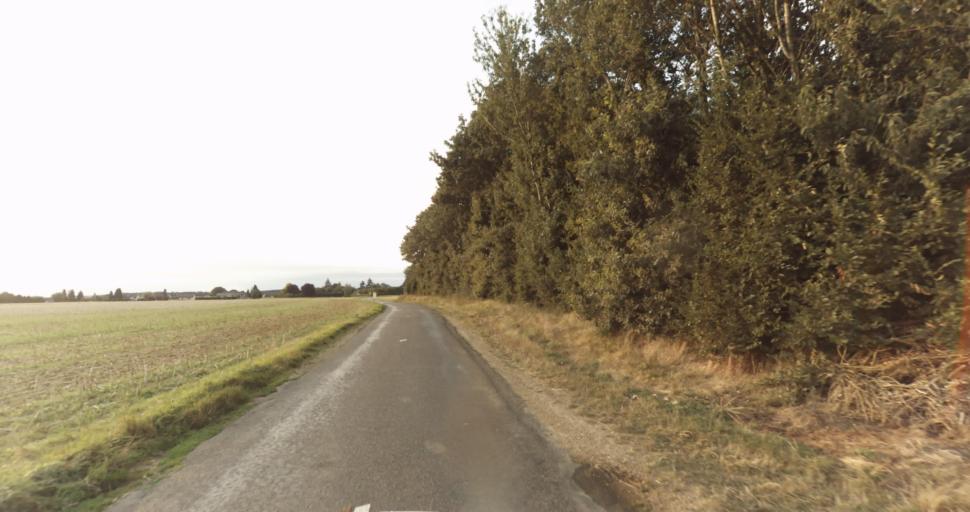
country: FR
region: Haute-Normandie
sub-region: Departement de l'Eure
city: La Madeleine-de-Nonancourt
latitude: 48.8778
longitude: 1.2430
